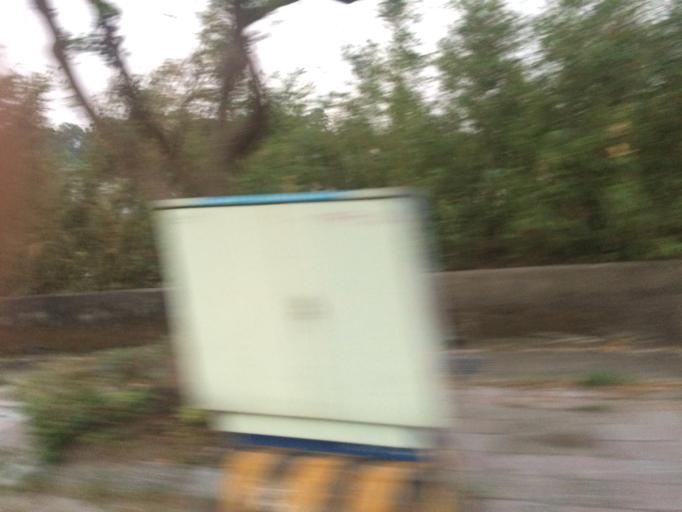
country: TW
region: Taiwan
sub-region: Hsinchu
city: Hsinchu
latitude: 24.7212
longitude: 120.9192
